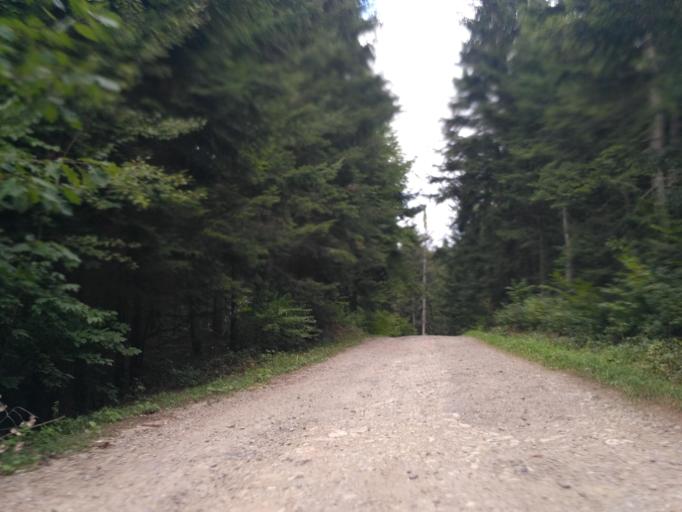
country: PL
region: Subcarpathian Voivodeship
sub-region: Powiat rzeszowski
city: Dynow
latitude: 49.7581
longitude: 22.2923
